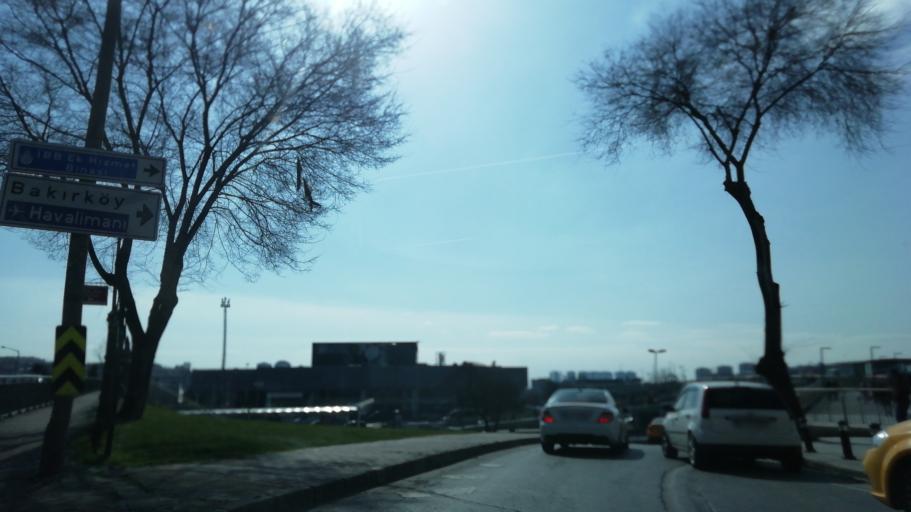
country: TR
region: Istanbul
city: guengoeren merter
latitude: 41.0039
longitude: 28.8903
